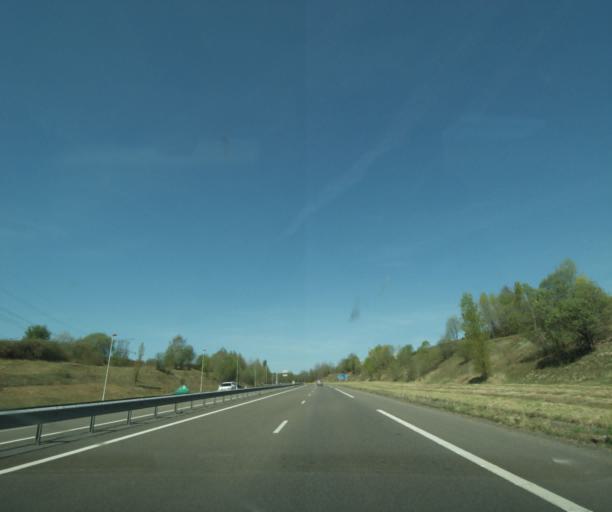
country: FR
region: Bourgogne
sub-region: Departement de la Nievre
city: Coulanges-les-Nevers
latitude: 47.0143
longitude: 3.2003
